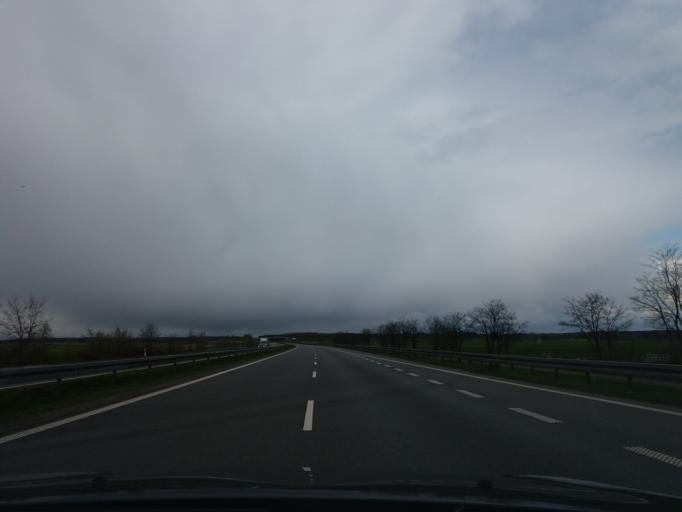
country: PL
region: Opole Voivodeship
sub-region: Powiat opolski
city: Proszkow
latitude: 50.5724
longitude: 17.8550
